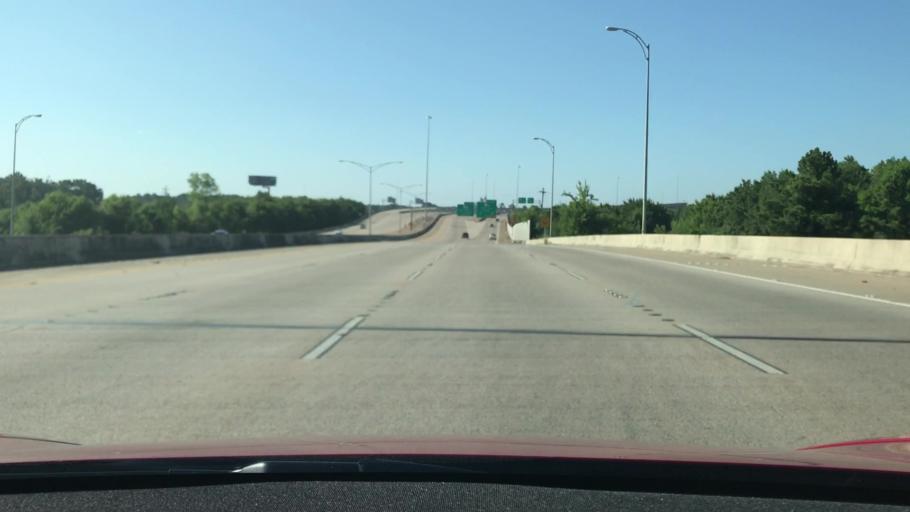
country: US
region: Louisiana
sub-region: Bossier Parish
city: Bossier City
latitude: 32.4278
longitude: -93.7526
